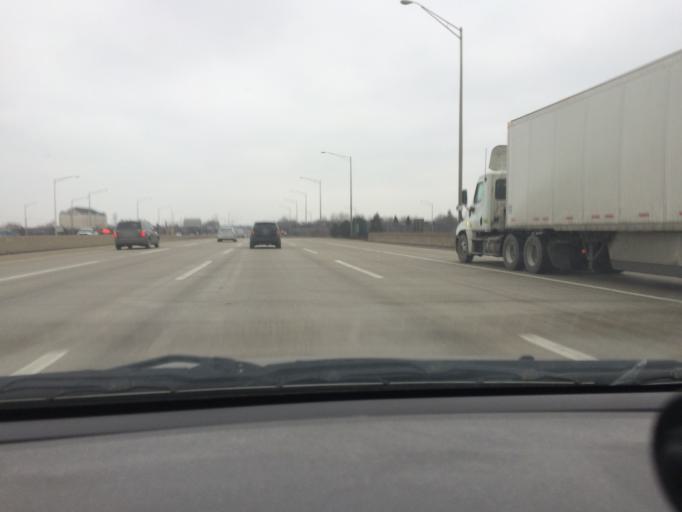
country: US
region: Illinois
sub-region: DuPage County
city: Glendale Heights
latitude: 41.9318
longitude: -88.0376
